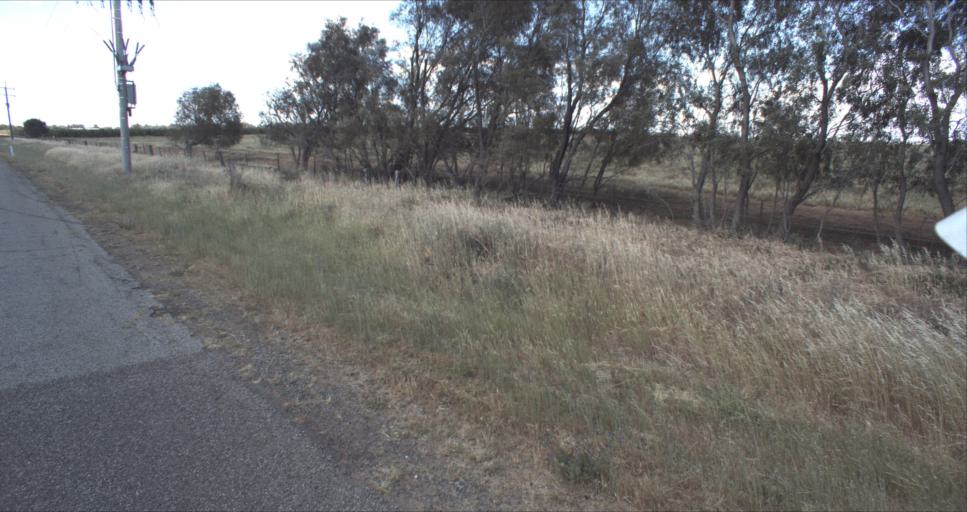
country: AU
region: New South Wales
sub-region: Leeton
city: Leeton
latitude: -34.5266
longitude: 146.2207
